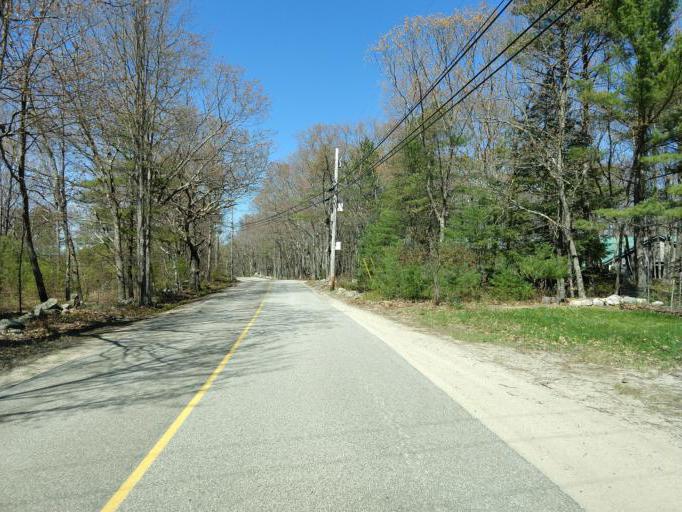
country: US
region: Maine
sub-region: York County
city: Arundel
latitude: 43.3942
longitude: -70.4526
